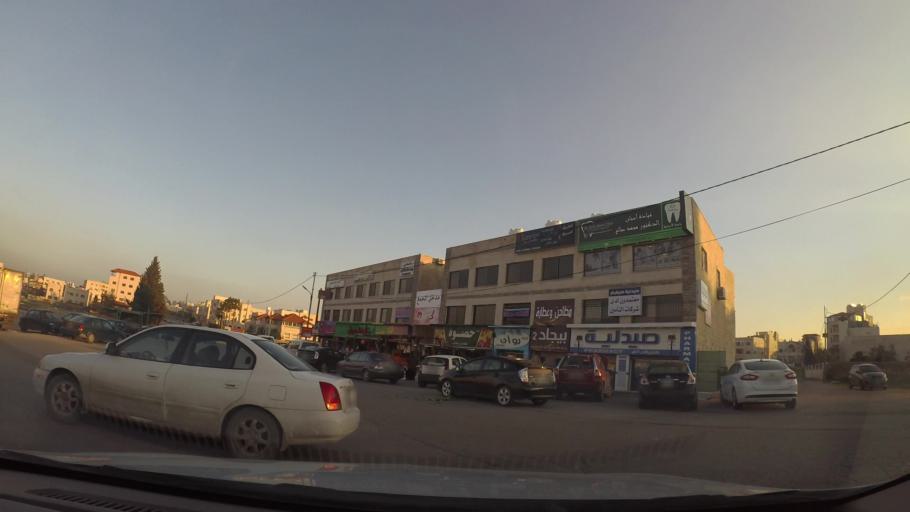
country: JO
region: Amman
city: Al Bunayyat ash Shamaliyah
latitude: 31.9050
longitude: 35.9199
